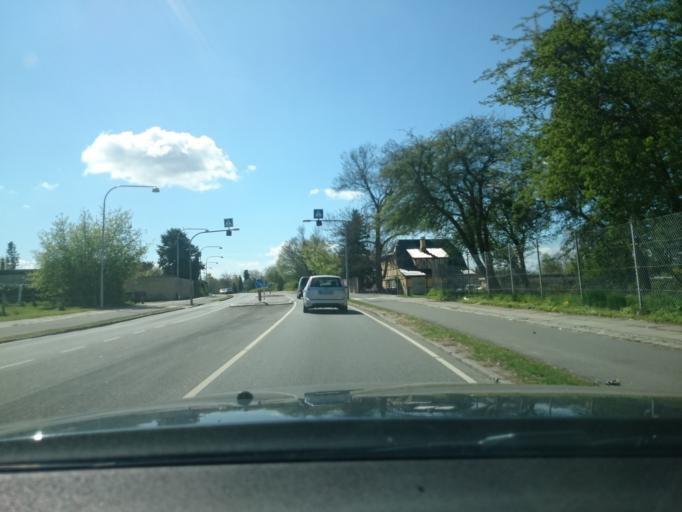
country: DK
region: Capital Region
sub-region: Lyngby-Tarbaek Kommune
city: Kongens Lyngby
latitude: 55.7775
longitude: 12.5368
